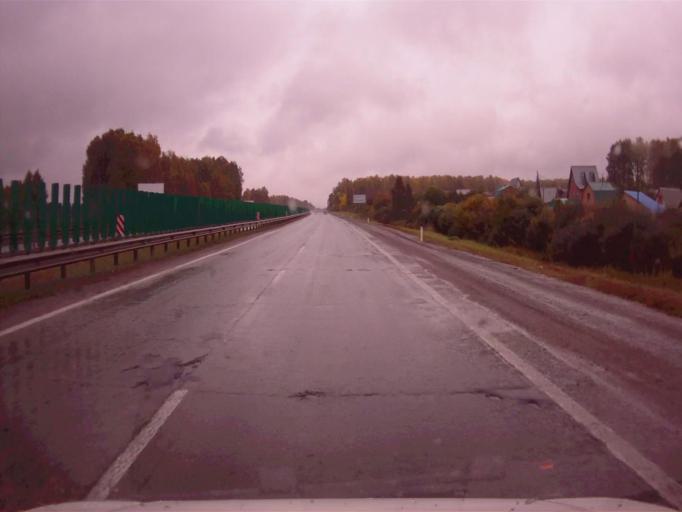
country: RU
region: Chelyabinsk
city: Dolgoderevenskoye
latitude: 55.3290
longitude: 61.3236
